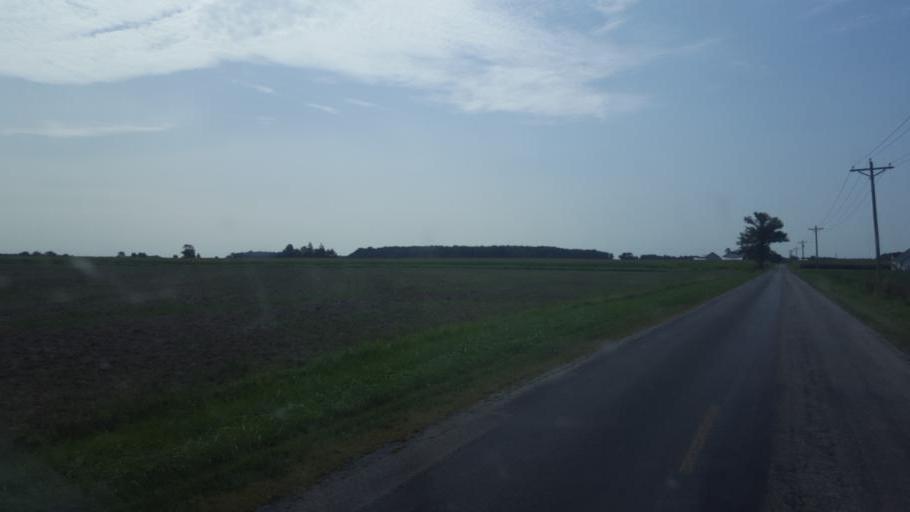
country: US
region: Ohio
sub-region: Morrow County
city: Cardington
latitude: 40.5188
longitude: -82.9956
